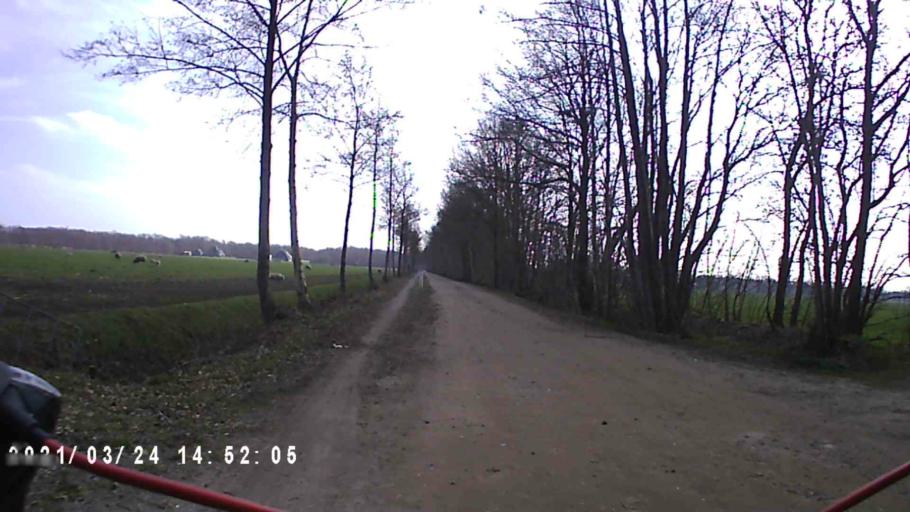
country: NL
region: Friesland
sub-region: Gemeente Heerenveen
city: Jubbega
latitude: 53.0293
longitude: 6.1010
